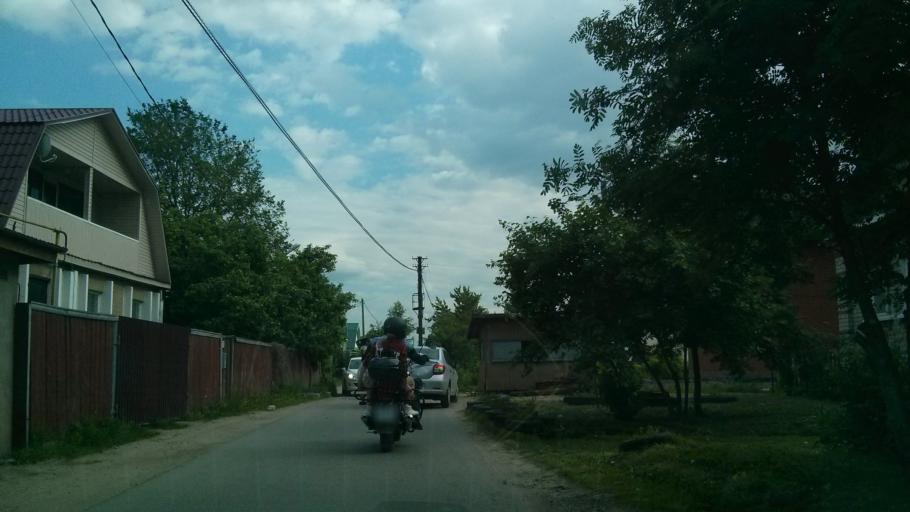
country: RU
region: Nizjnij Novgorod
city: Afonino
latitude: 56.2875
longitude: 44.0998
